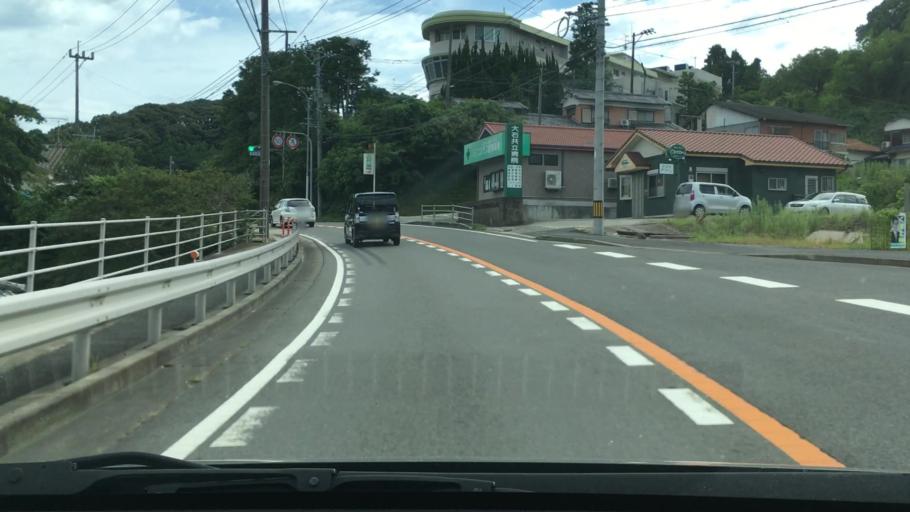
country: JP
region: Nagasaki
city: Togitsu
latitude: 32.8822
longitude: 129.7894
